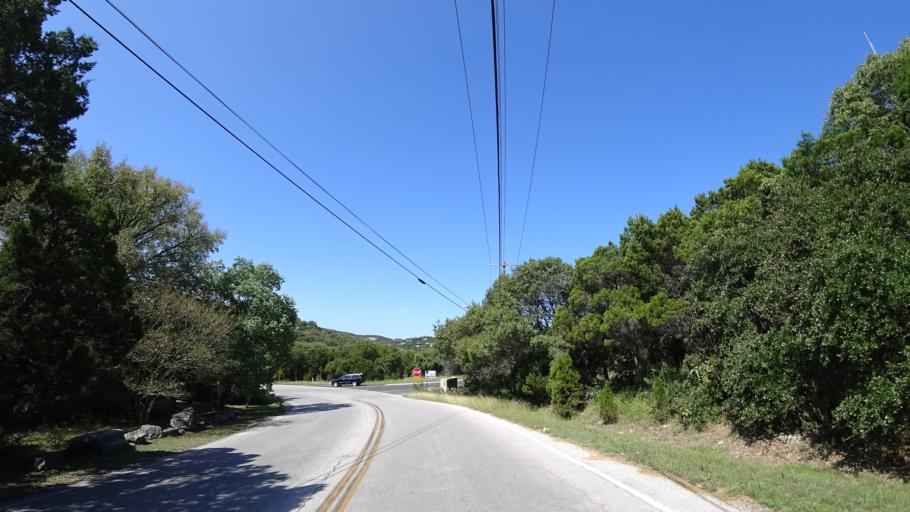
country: US
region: Texas
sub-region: Travis County
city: West Lake Hills
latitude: 30.3044
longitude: -97.7947
